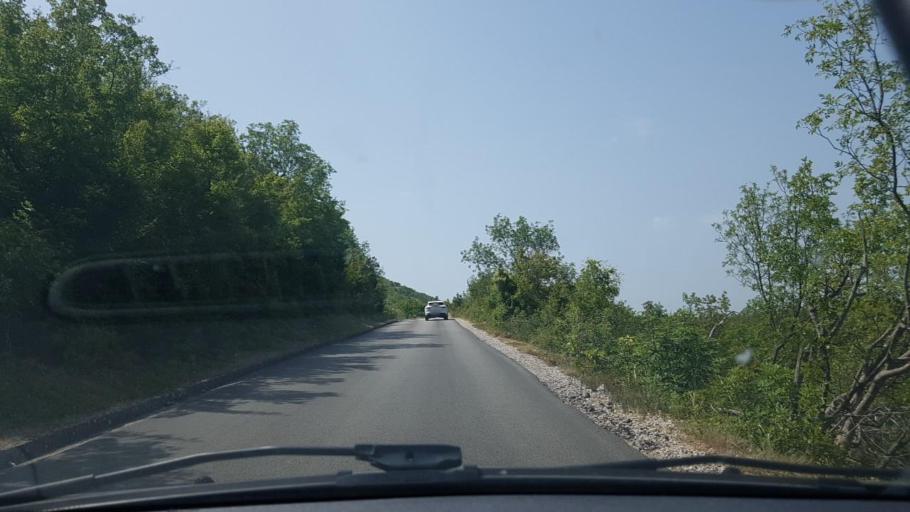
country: HR
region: Dubrovacko-Neretvanska
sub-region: Grad Dubrovnik
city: Metkovic
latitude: 43.0386
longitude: 17.7156
